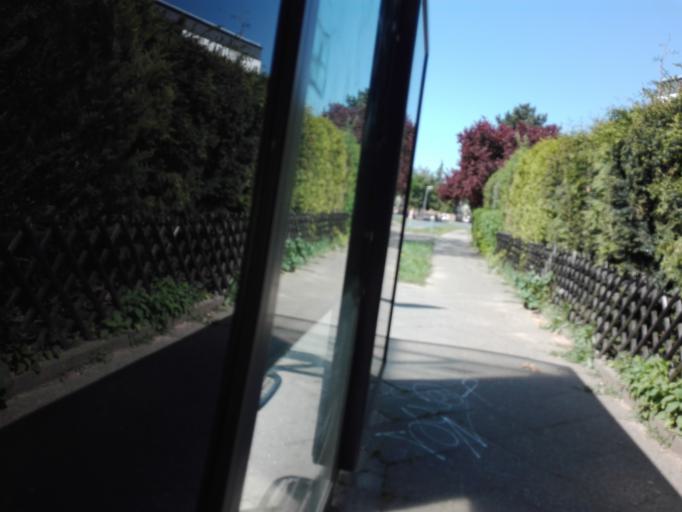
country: DE
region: Berlin
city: Rudow
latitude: 52.4010
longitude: 13.4860
